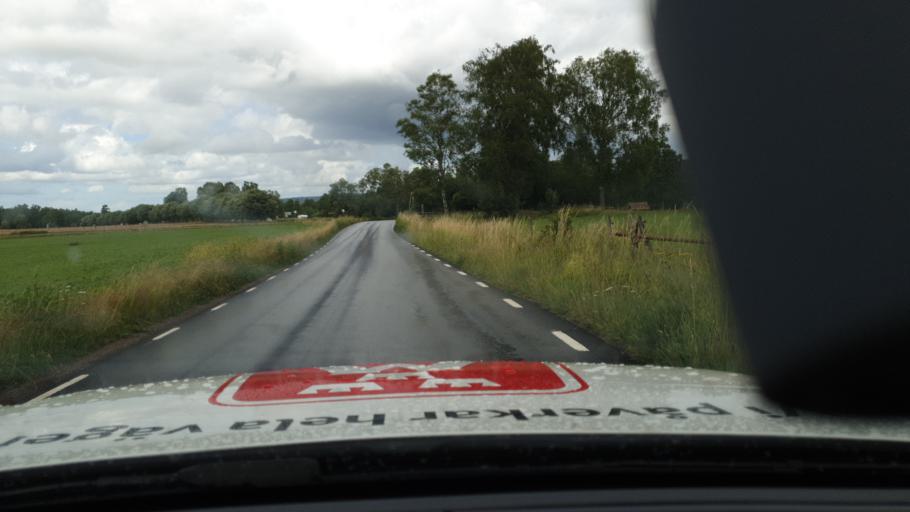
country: SE
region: Vaestra Goetaland
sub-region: Falkopings Kommun
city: Akarp
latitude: 58.2758
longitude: 13.6048
